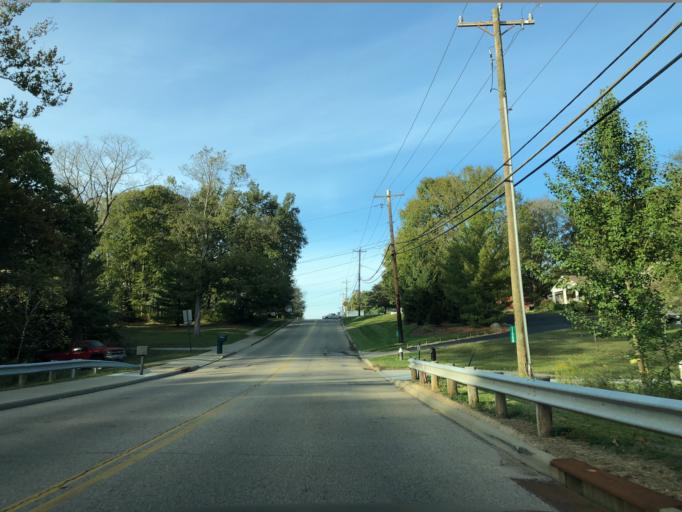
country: US
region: Ohio
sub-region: Hamilton County
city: Loveland
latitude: 39.2724
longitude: -84.2735
